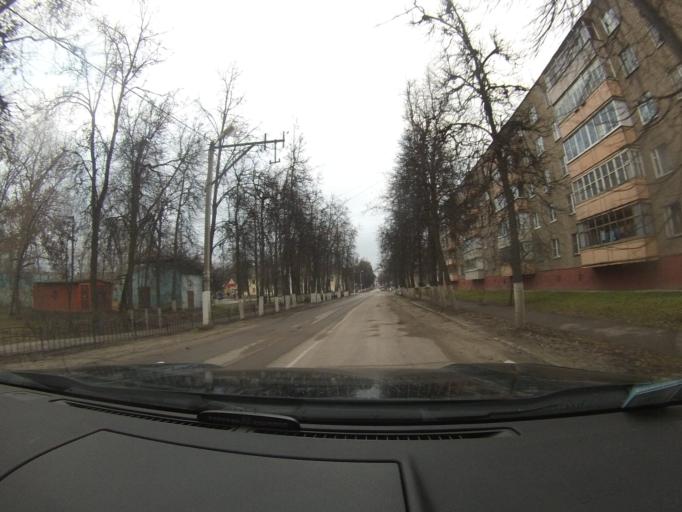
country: RU
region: Moskovskaya
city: Peski
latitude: 55.2510
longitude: 38.7605
